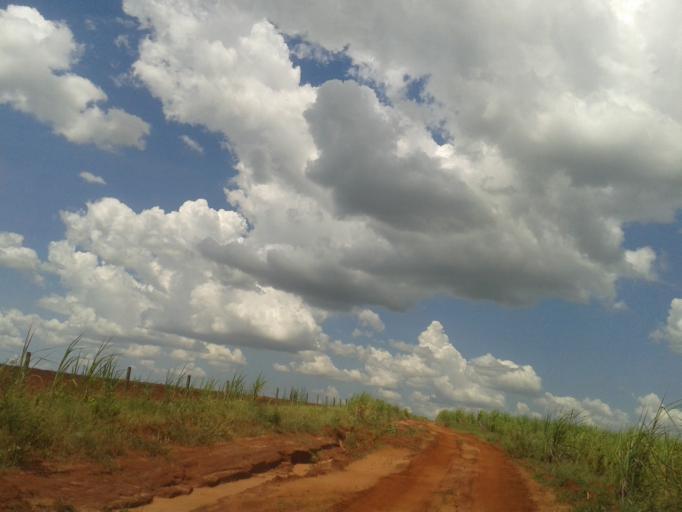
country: BR
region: Minas Gerais
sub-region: Santa Vitoria
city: Santa Vitoria
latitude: -19.1718
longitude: -50.4327
